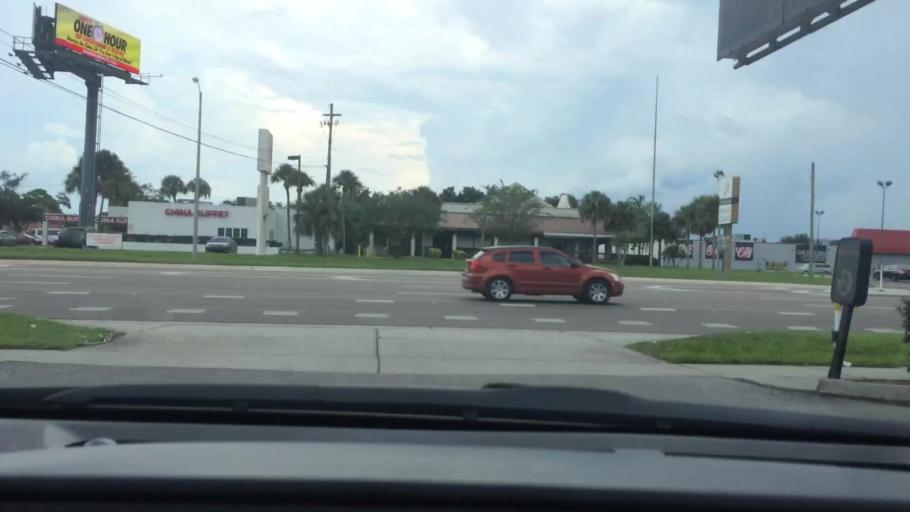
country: US
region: Florida
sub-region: Hillsborough County
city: University
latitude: 28.0549
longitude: -82.4466
